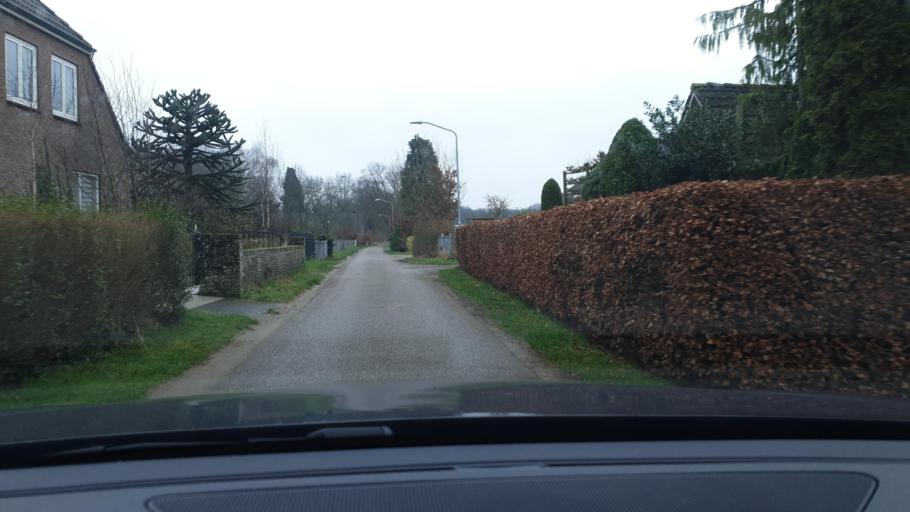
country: NL
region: North Brabant
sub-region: Gemeente Veldhoven
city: Oerle
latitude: 51.4001
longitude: 5.3810
